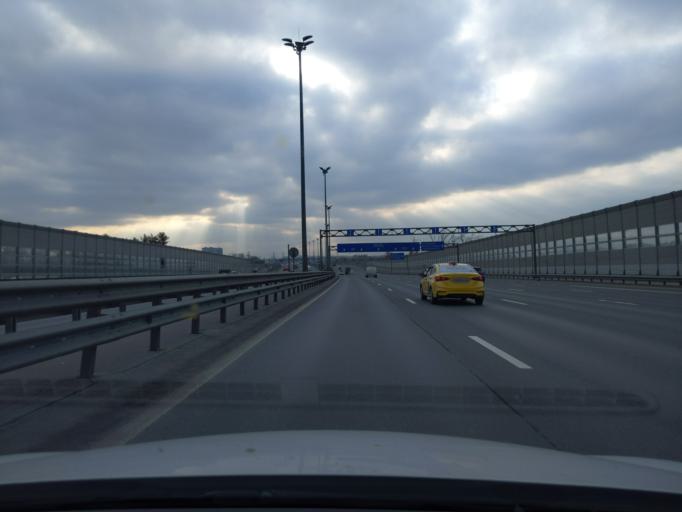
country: RU
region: Moskovskaya
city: Lesnyye Polyany
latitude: 55.9701
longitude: 37.8458
